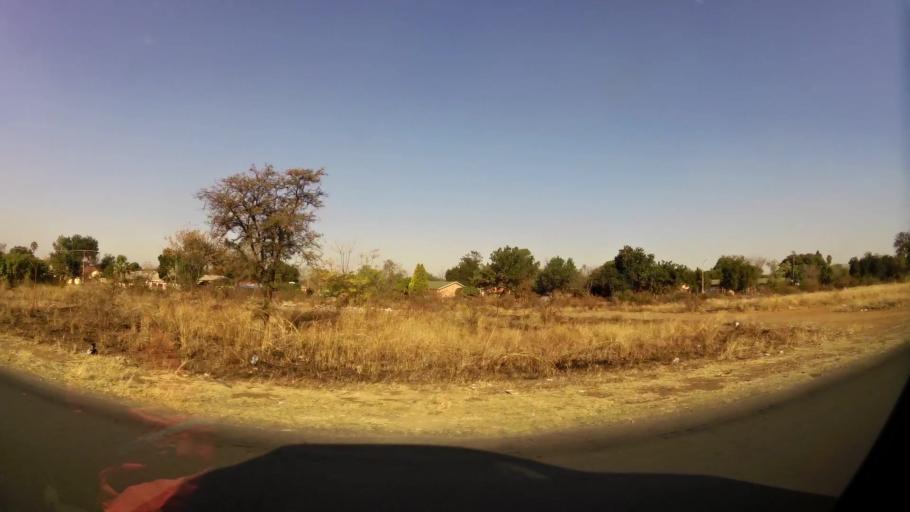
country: ZA
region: North-West
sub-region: Bojanala Platinum District Municipality
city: Rustenburg
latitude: -25.6521
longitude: 27.2218
